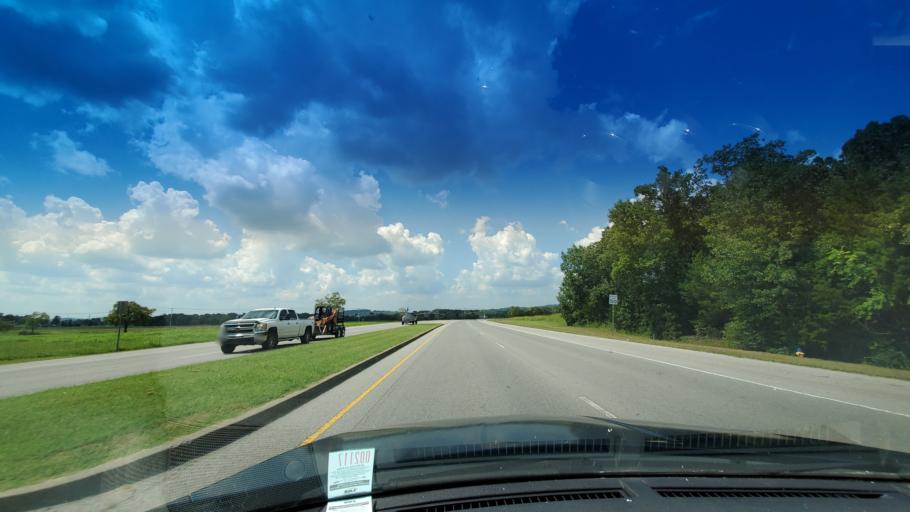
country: US
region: Tennessee
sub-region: Wilson County
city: Lebanon
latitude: 36.1765
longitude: -86.3188
